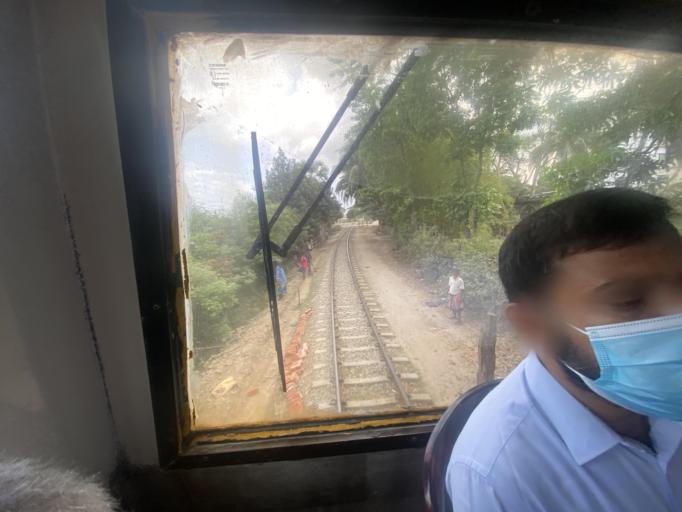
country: BD
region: Chittagong
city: Chittagong
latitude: 22.3333
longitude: 91.7704
